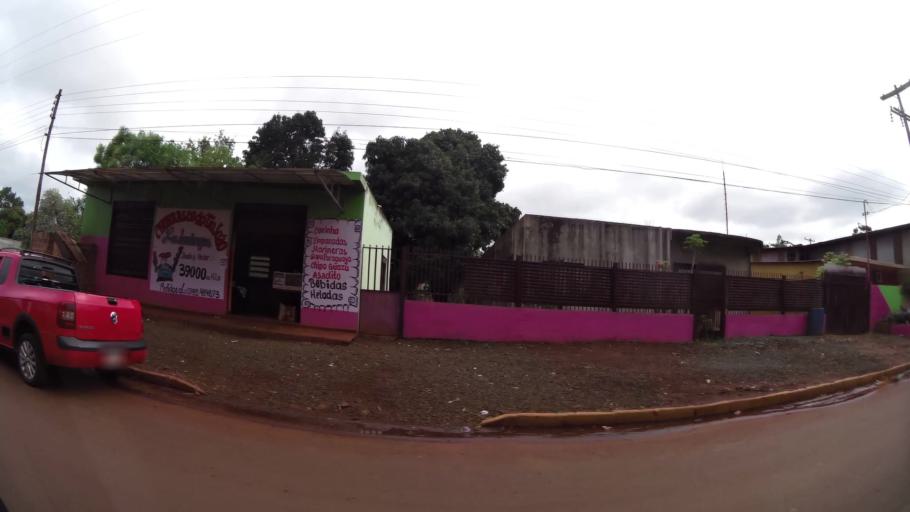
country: PY
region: Alto Parana
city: Ciudad del Este
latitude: -25.3826
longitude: -54.6480
